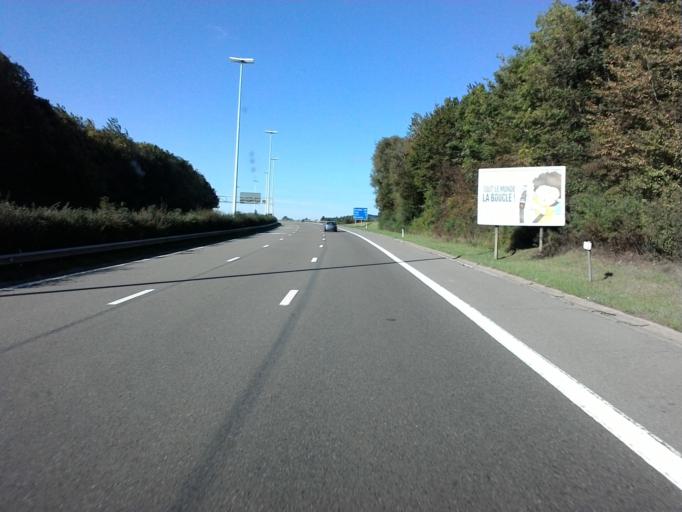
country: BE
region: Wallonia
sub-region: Province du Luxembourg
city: Aubange
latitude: 49.5693
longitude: 5.8216
